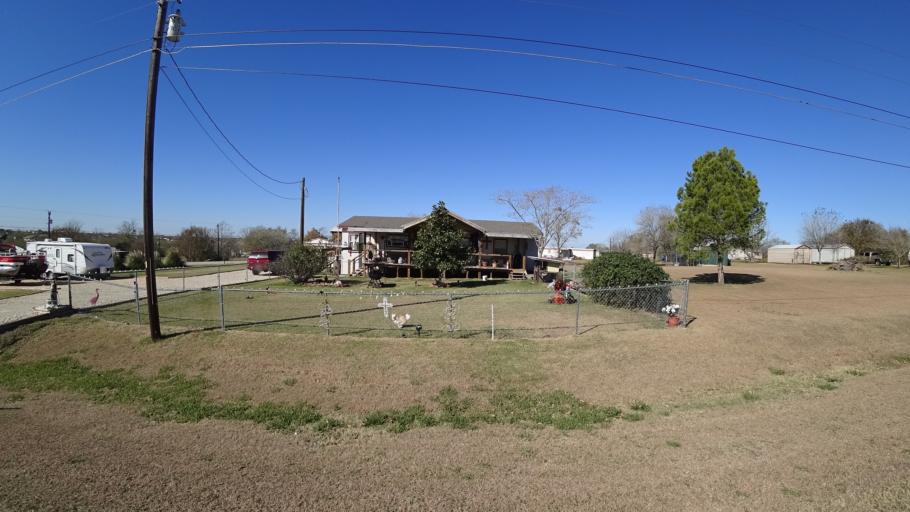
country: US
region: Texas
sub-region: Travis County
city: Garfield
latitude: 30.1038
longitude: -97.5964
